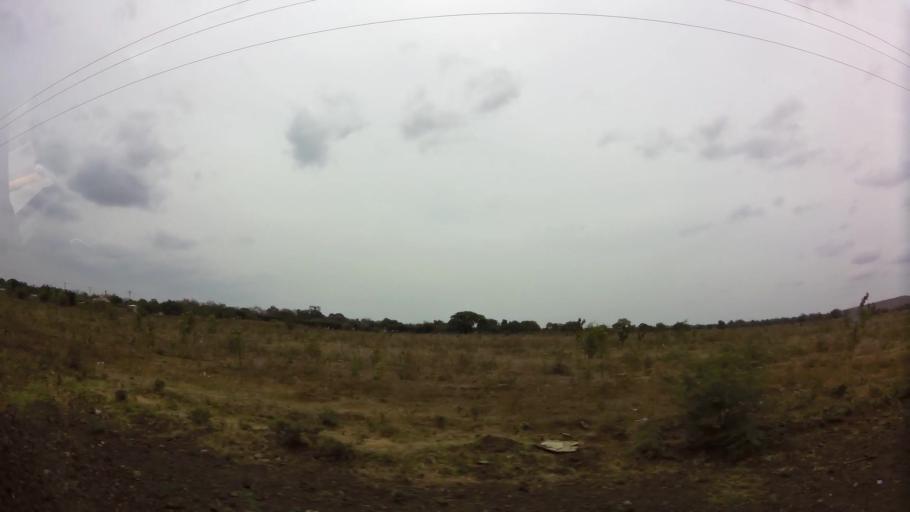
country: NI
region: Managua
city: Managua
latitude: 12.1151
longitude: -86.1720
